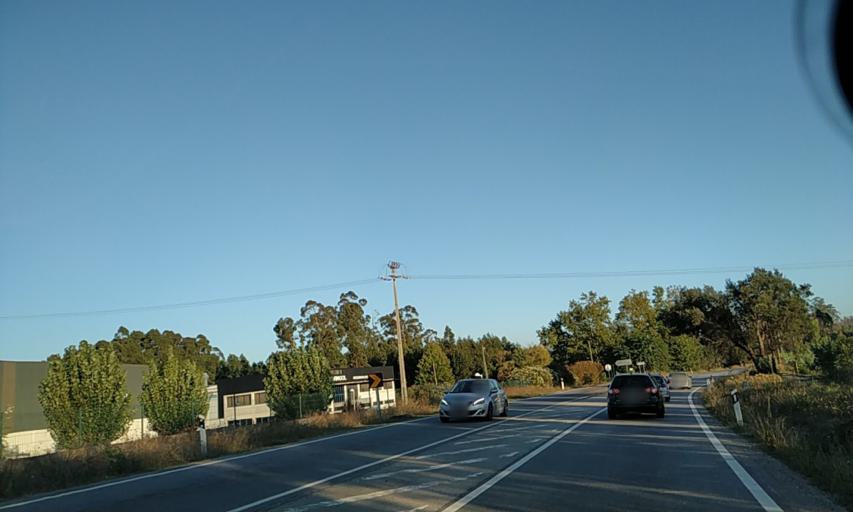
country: PT
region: Aveiro
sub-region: Oliveira do Bairro
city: Oia
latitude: 40.5657
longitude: -8.5643
